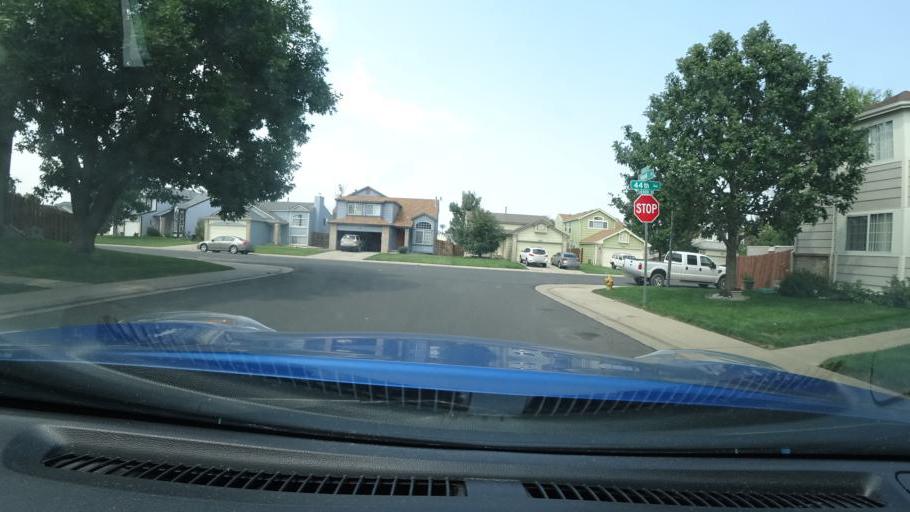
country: US
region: Colorado
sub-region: Adams County
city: Aurora
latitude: 39.7773
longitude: -104.7410
